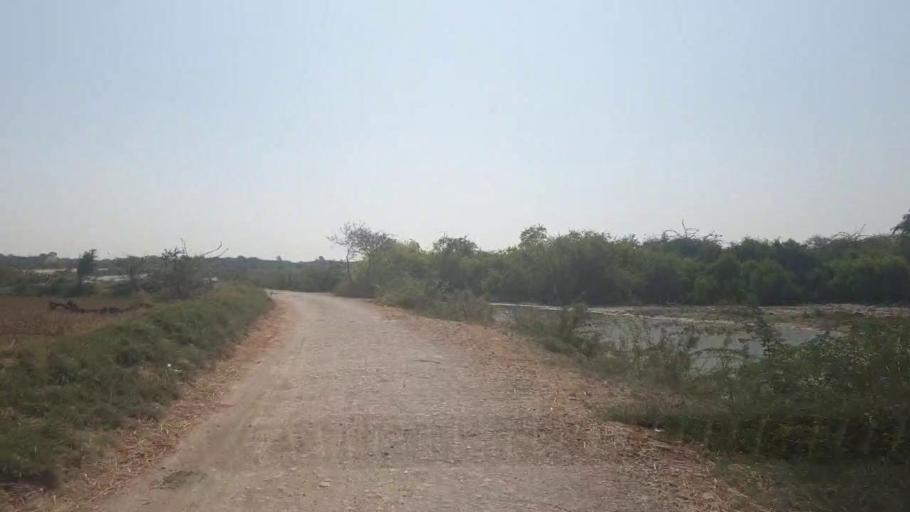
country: PK
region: Sindh
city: Badin
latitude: 24.6517
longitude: 68.9163
